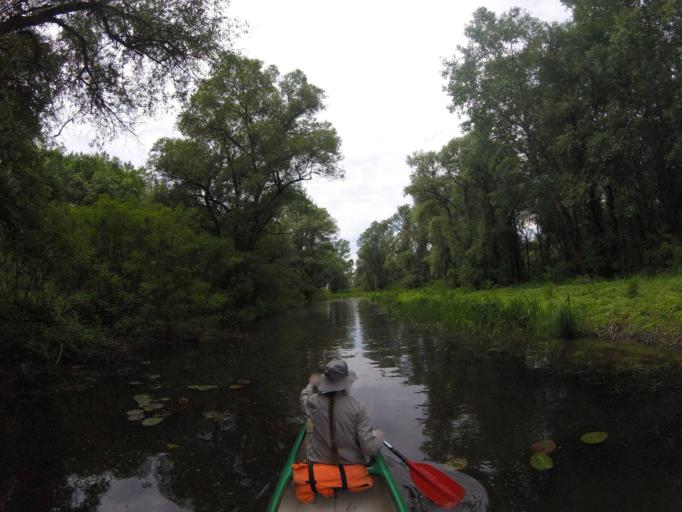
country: HU
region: Szabolcs-Szatmar-Bereg
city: Rakamaz
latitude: 48.1637
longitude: 21.4342
